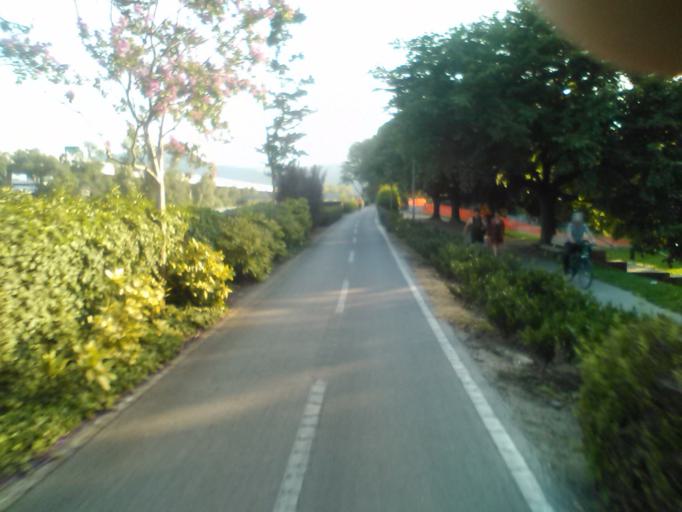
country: IT
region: Trentino-Alto Adige
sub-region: Bolzano
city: Bolzano
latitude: 46.4848
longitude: 11.3265
